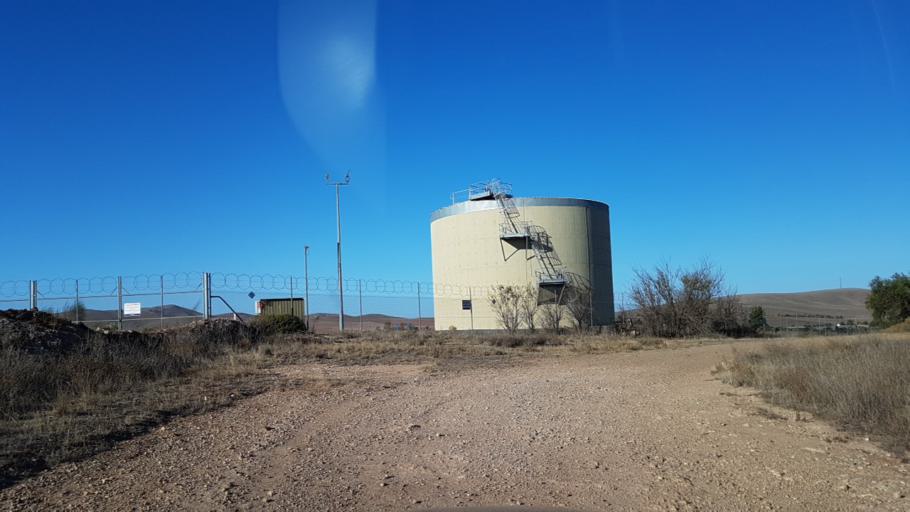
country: AU
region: South Australia
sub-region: Clare and Gilbert Valleys
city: Clare
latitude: -33.6756
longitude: 138.9270
